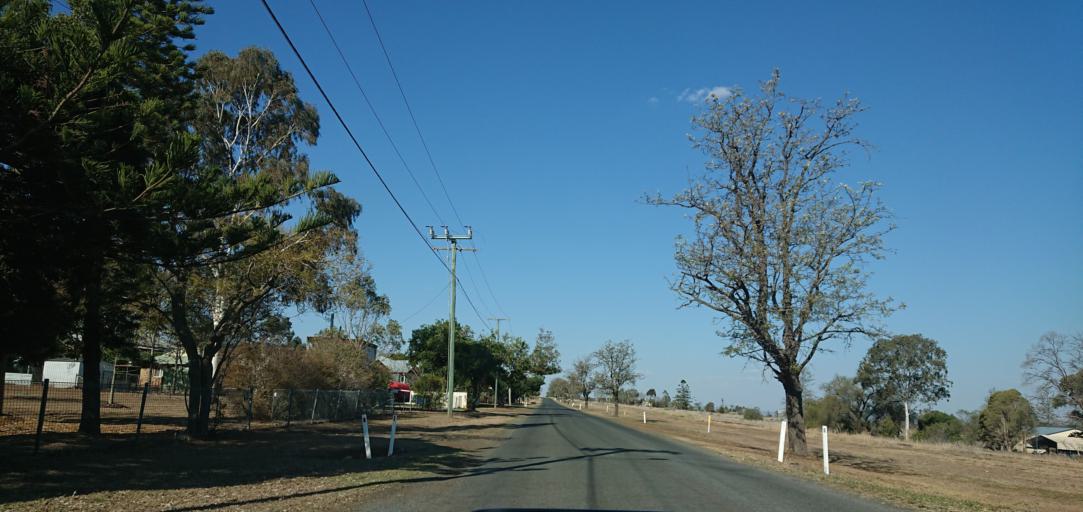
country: AU
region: Queensland
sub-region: Toowoomba
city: Westbrook
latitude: -27.6784
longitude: 151.7144
